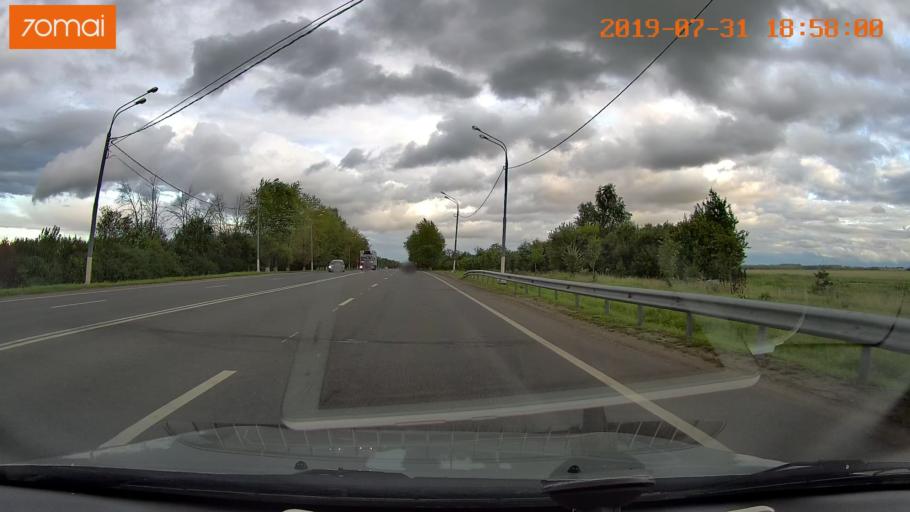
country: RU
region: Moskovskaya
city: Raduzhnyy
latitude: 55.1500
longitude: 38.6990
